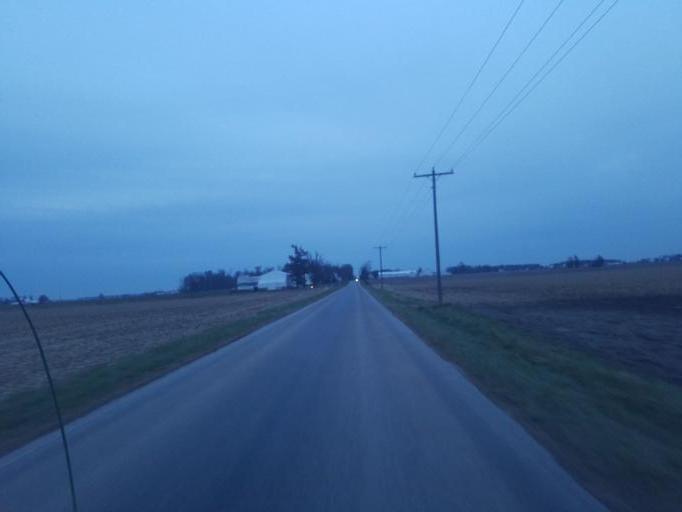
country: US
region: Indiana
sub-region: Adams County
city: Berne
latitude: 40.7316
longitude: -84.9346
